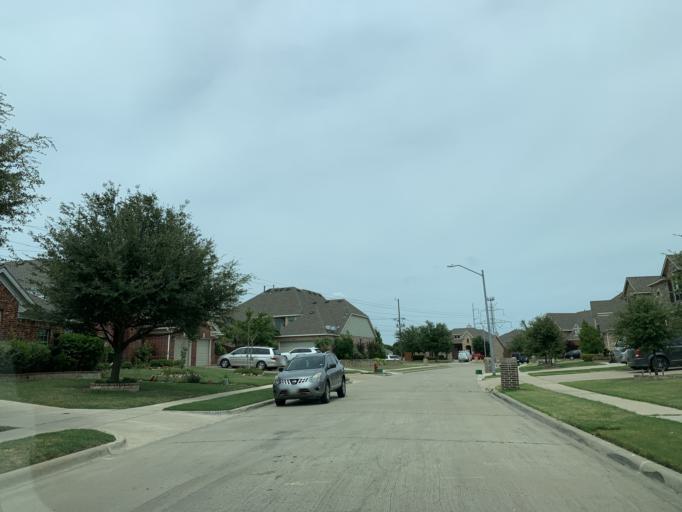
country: US
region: Texas
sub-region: Dallas County
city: Grand Prairie
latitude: 32.6541
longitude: -97.0373
